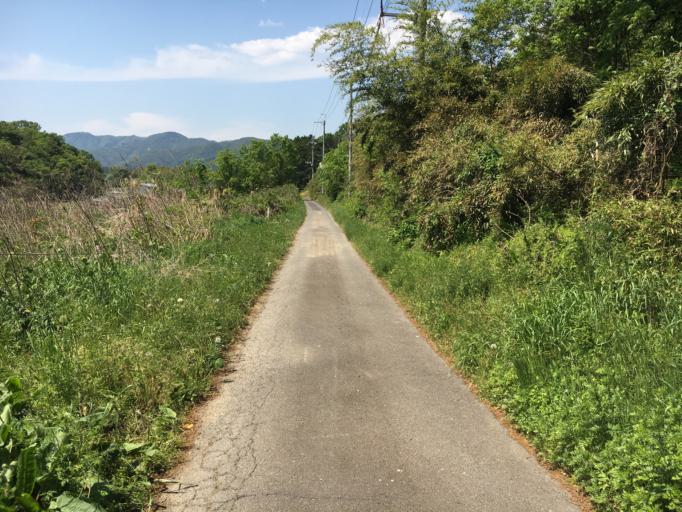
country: JP
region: Kyoto
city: Kameoka
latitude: 35.0697
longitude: 135.5700
